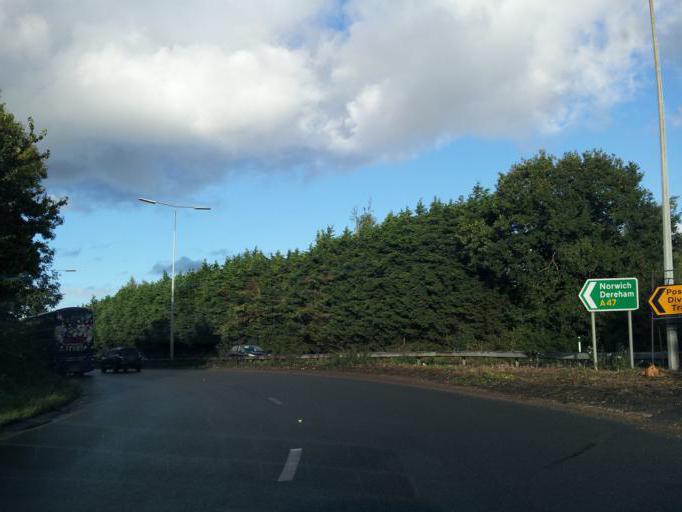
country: GB
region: England
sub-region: Norfolk
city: Brundall
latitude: 52.6314
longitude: 1.4253
